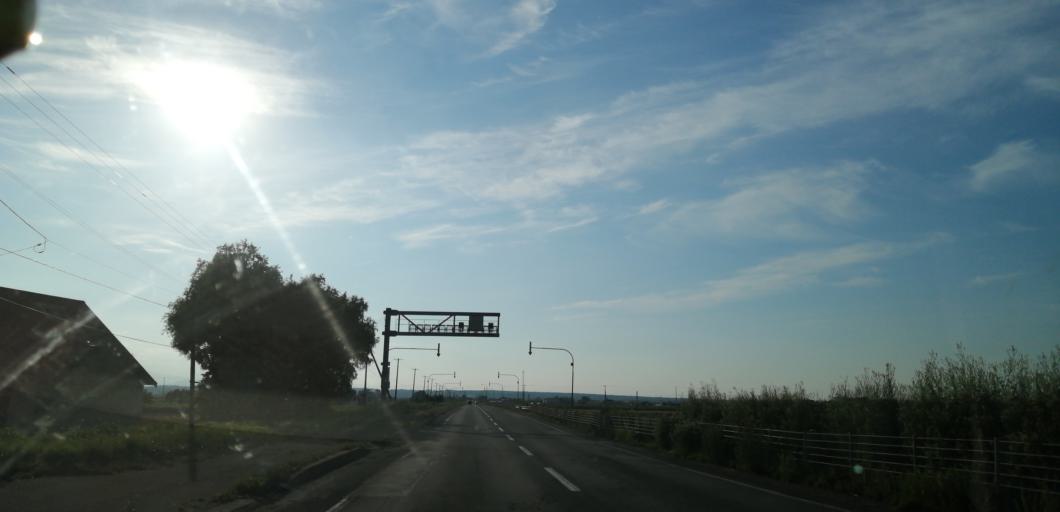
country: JP
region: Hokkaido
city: Kitahiroshima
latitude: 42.9900
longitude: 141.6078
